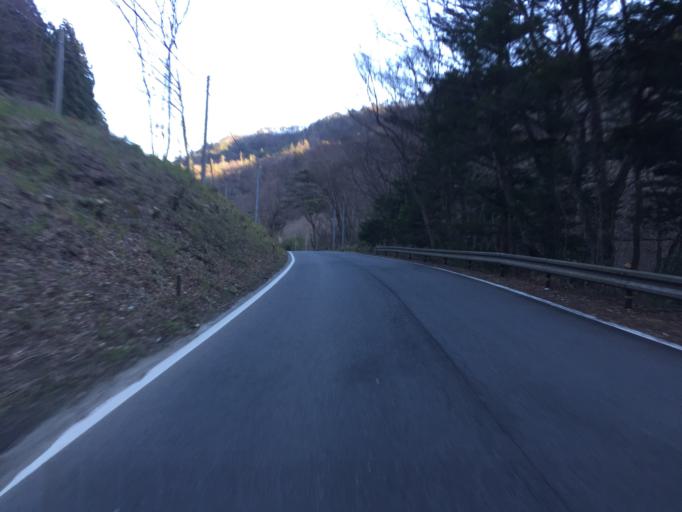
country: JP
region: Fukushima
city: Iwaki
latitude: 37.1915
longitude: 140.7957
